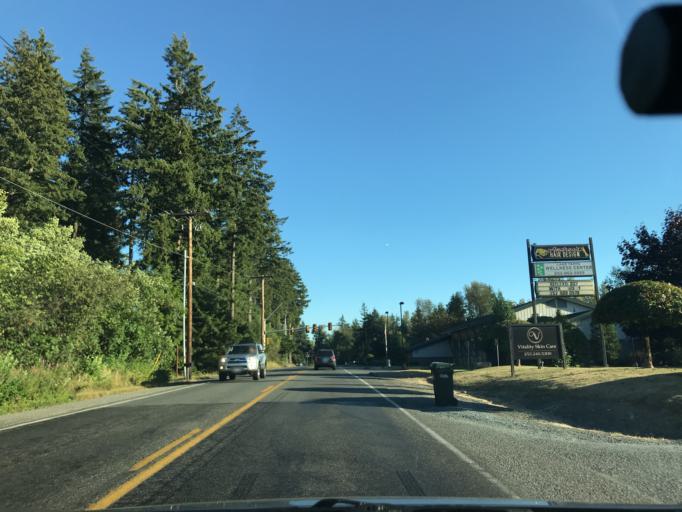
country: US
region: Washington
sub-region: King County
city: Pacific
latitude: 47.2546
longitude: -122.1869
